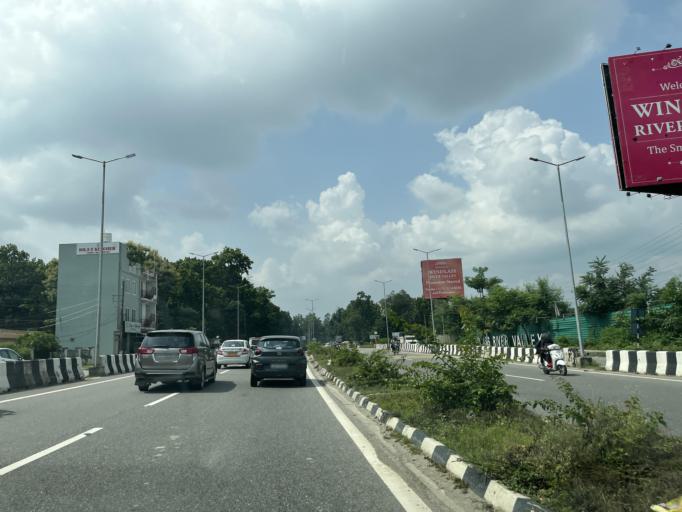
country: IN
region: Uttarakhand
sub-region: Dehradun
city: Raipur
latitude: 30.2474
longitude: 78.0963
